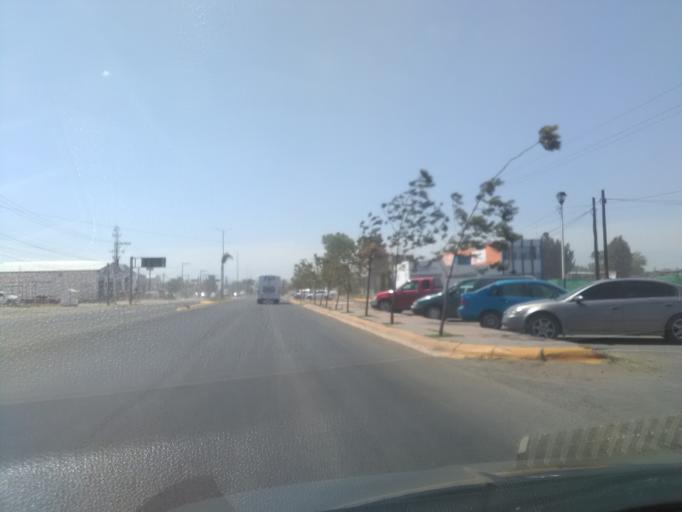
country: MX
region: Durango
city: Victoria de Durango
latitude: 24.0302
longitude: -104.6099
